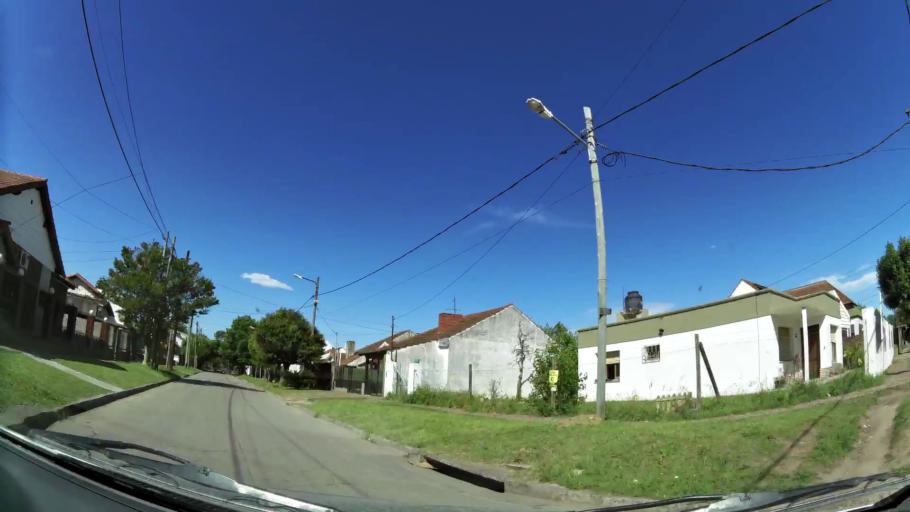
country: AR
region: Buenos Aires
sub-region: Partido de Almirante Brown
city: Adrogue
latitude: -34.7995
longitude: -58.3588
